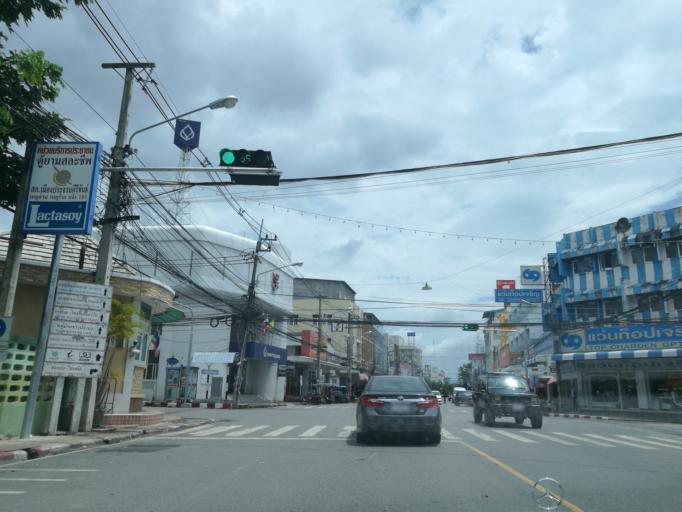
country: TH
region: Prachuap Khiri Khan
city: Prachuap Khiri Khan
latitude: 11.8038
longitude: 99.7975
